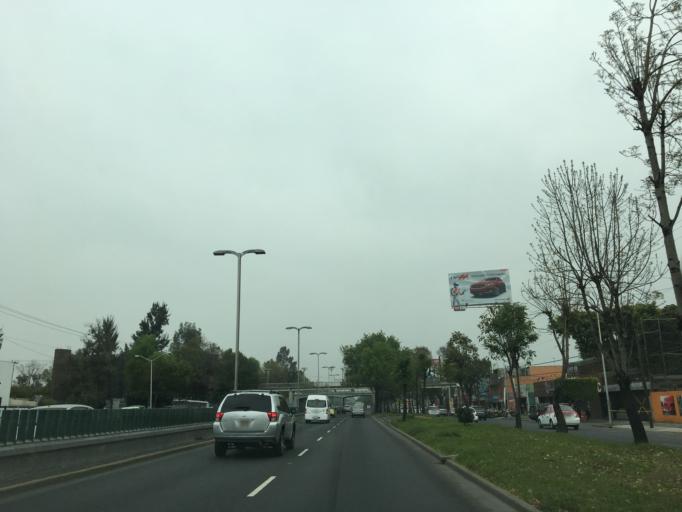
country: MX
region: Mexico City
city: Tlalpan
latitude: 19.2984
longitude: -99.1453
